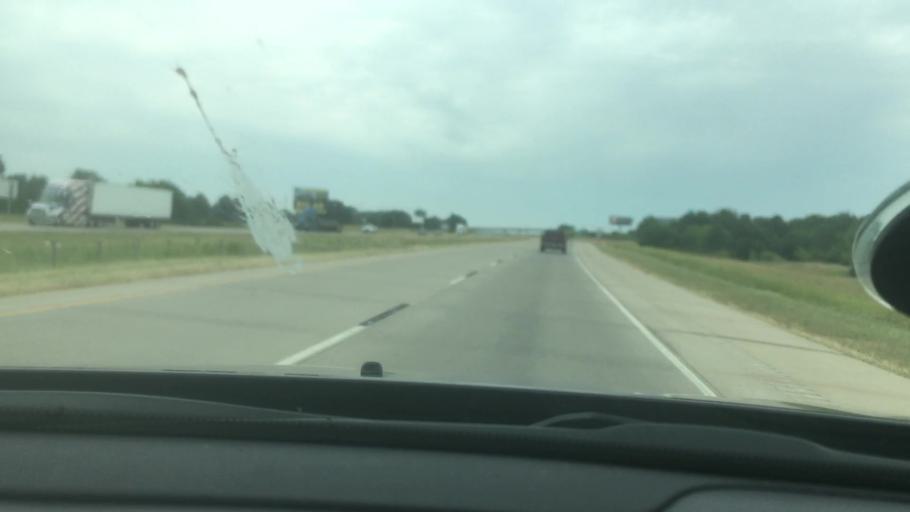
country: US
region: Oklahoma
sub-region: Carter County
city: Ardmore
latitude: 34.3109
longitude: -97.1584
